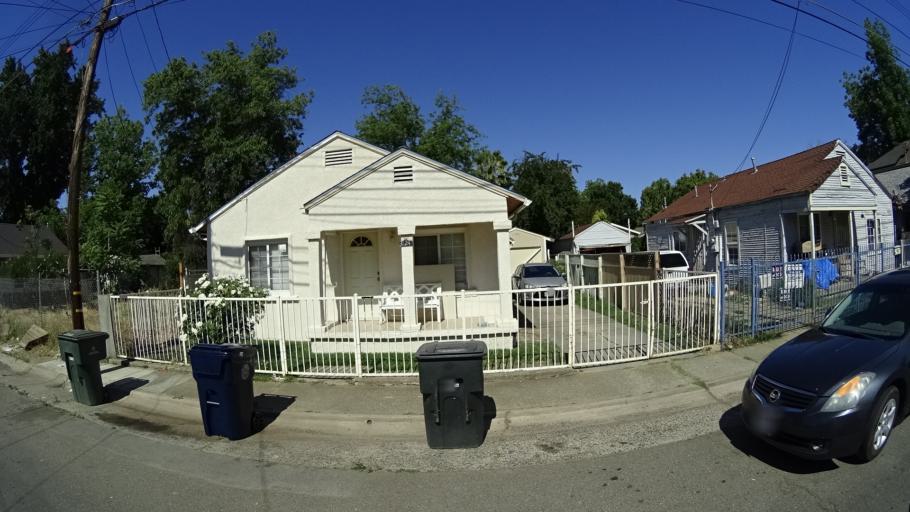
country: US
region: California
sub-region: Sacramento County
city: Parkway
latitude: 38.5455
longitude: -121.4559
